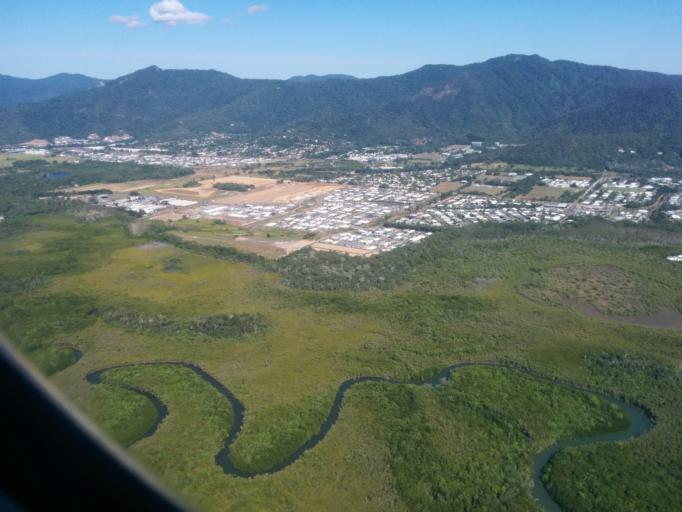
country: AU
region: Queensland
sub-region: Cairns
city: Yorkeys Knob
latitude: -16.8114
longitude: 145.7191
